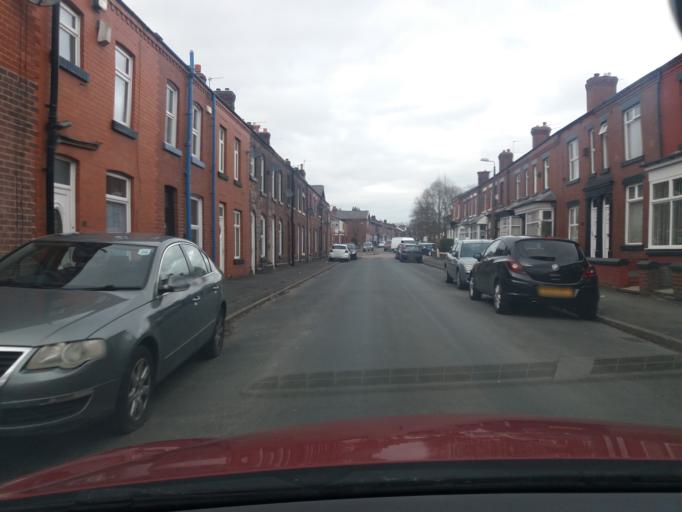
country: GB
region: England
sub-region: Lancashire
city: Chorley
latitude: 53.6585
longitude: -2.6261
